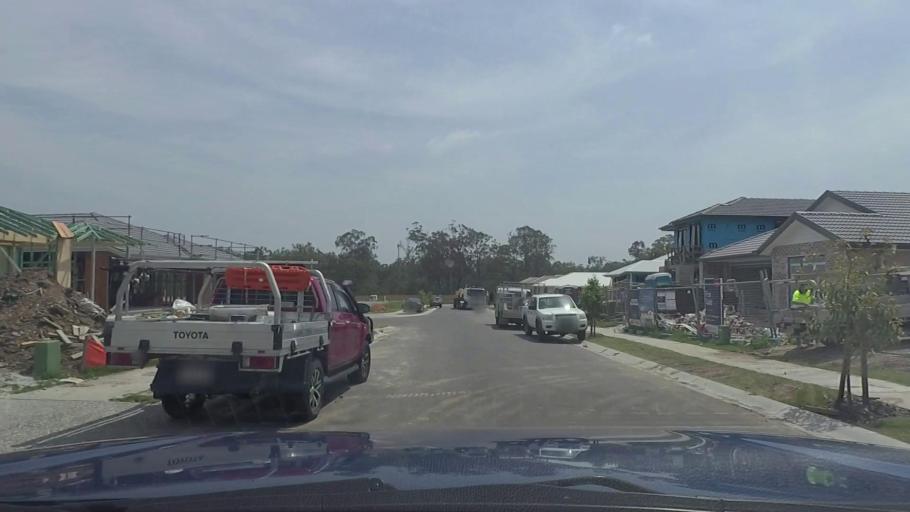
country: AU
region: Queensland
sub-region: Logan
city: Logan Reserve
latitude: -27.7045
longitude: 153.1050
